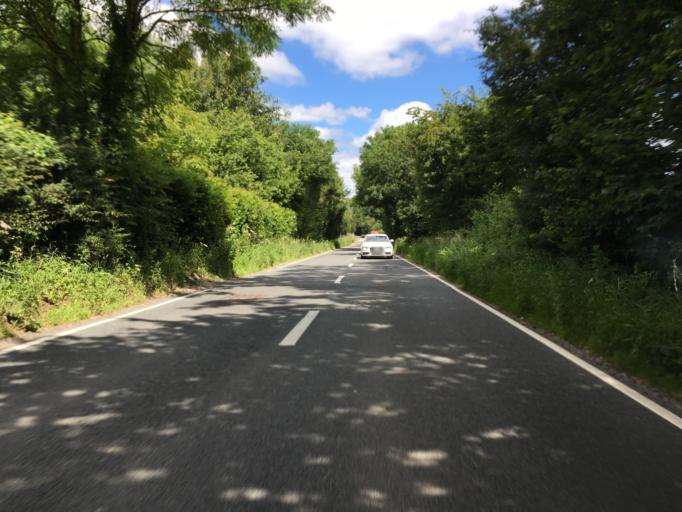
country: GB
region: England
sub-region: Hampshire
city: Highclere
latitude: 51.3265
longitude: -1.3806
